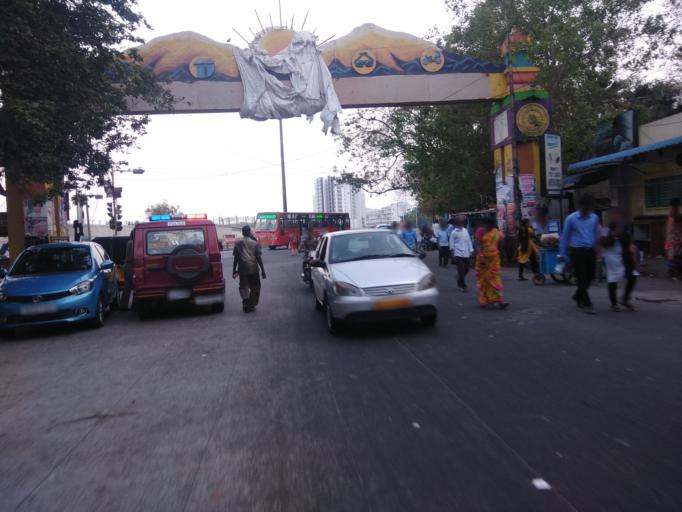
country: IN
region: Tamil Nadu
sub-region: Kancheepuram
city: Alandur
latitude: 13.0202
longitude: 80.2245
